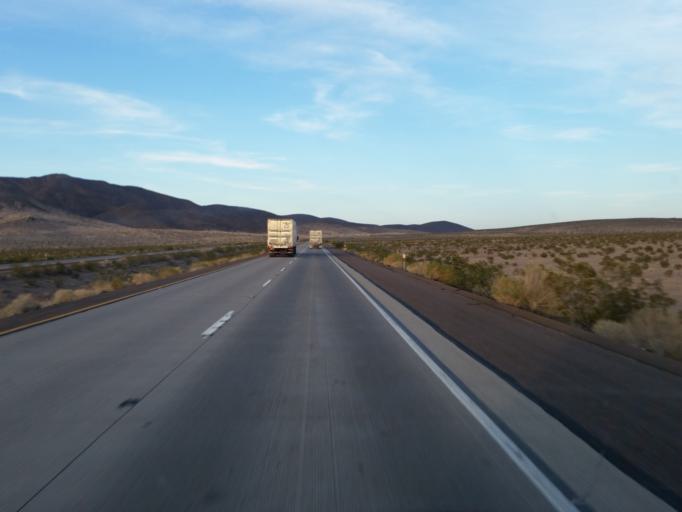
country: US
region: California
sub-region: San Bernardino County
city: Twentynine Palms
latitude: 34.7271
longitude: -116.1031
